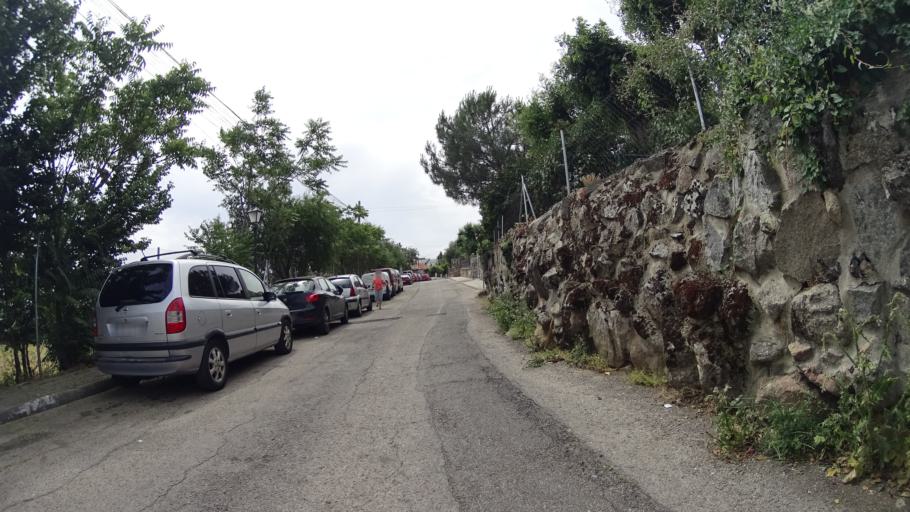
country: ES
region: Madrid
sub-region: Provincia de Madrid
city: Galapagar
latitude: 40.5742
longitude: -4.0004
